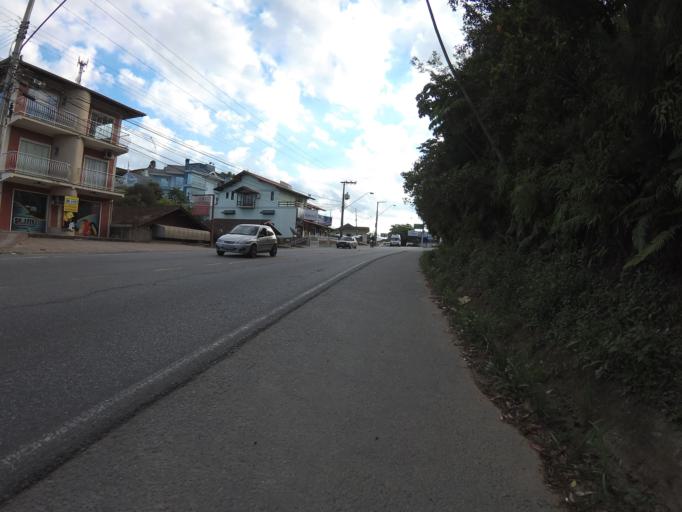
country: BR
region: Santa Catarina
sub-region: Blumenau
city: Blumenau
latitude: -26.8688
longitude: -49.0910
